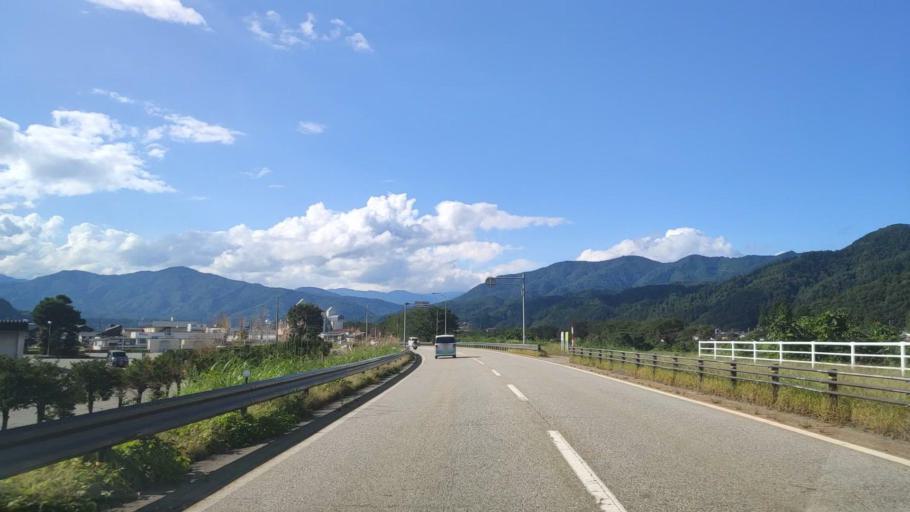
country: JP
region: Gifu
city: Takayama
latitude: 36.2445
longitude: 137.1712
